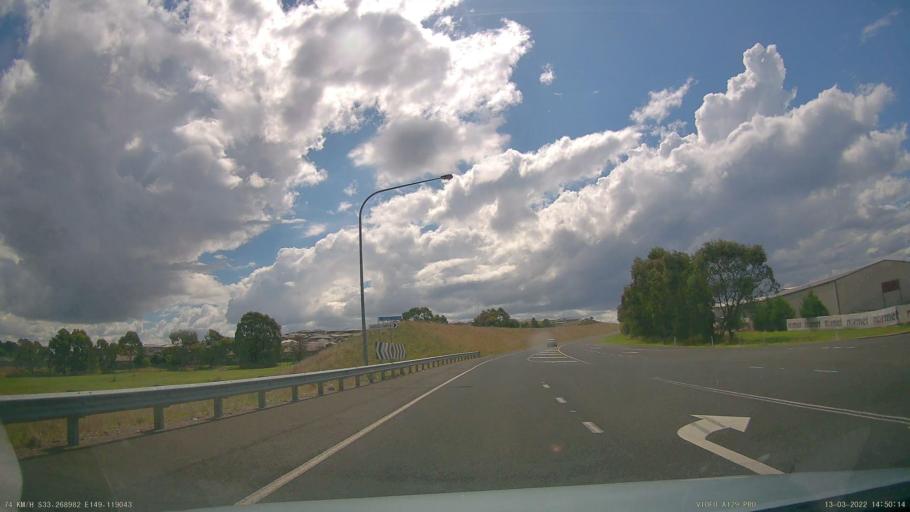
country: AU
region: New South Wales
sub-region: Orange Municipality
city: Orange
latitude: -33.2688
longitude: 149.1189
